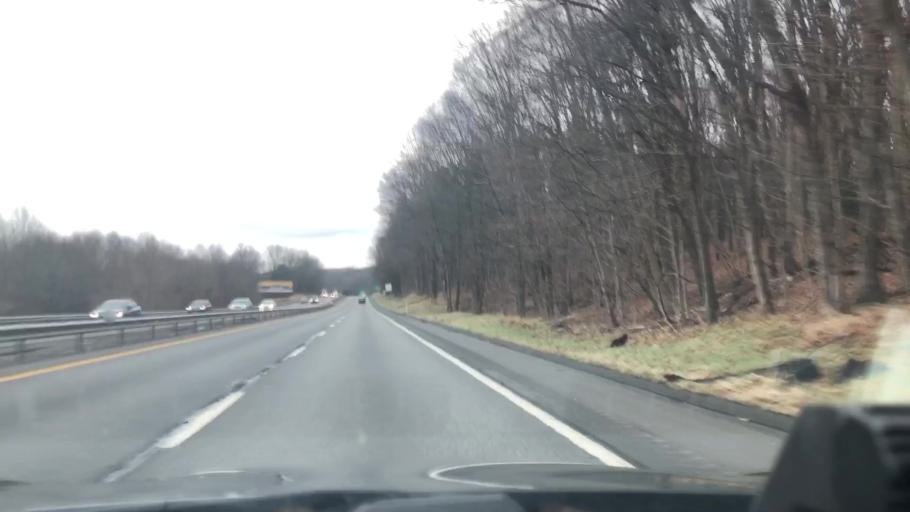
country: US
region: Pennsylvania
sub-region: Monroe County
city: Saylorsburg
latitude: 40.8981
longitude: -75.3088
